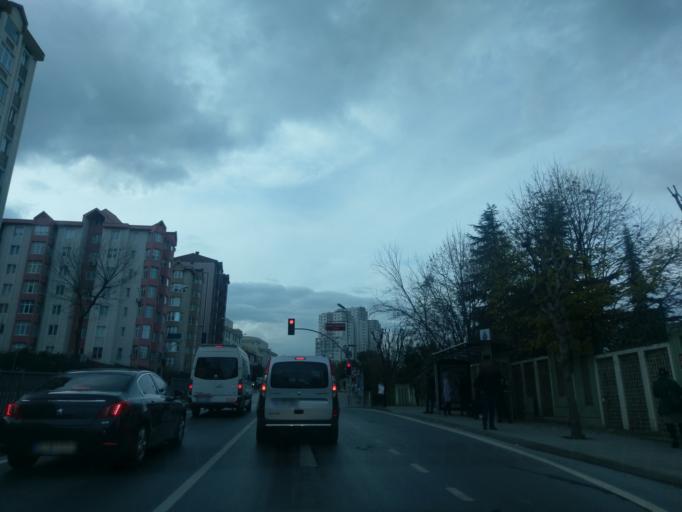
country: TR
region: Istanbul
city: Esenyurt
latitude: 41.0637
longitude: 28.6759
